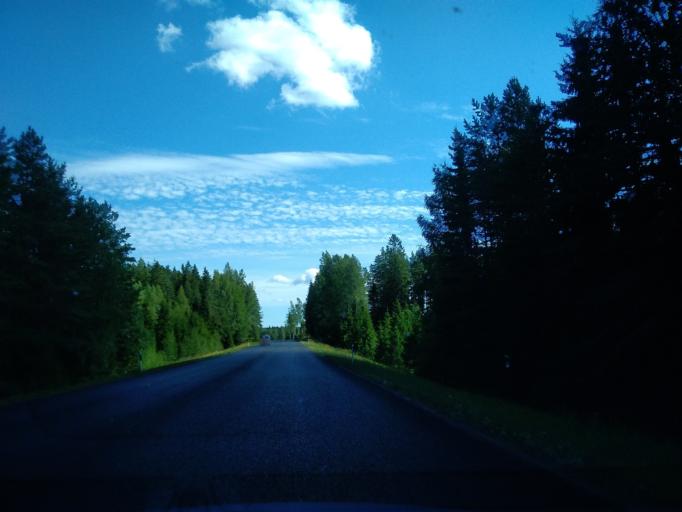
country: FI
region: Haeme
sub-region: Haemeenlinna
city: Renko
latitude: 60.9387
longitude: 24.3794
